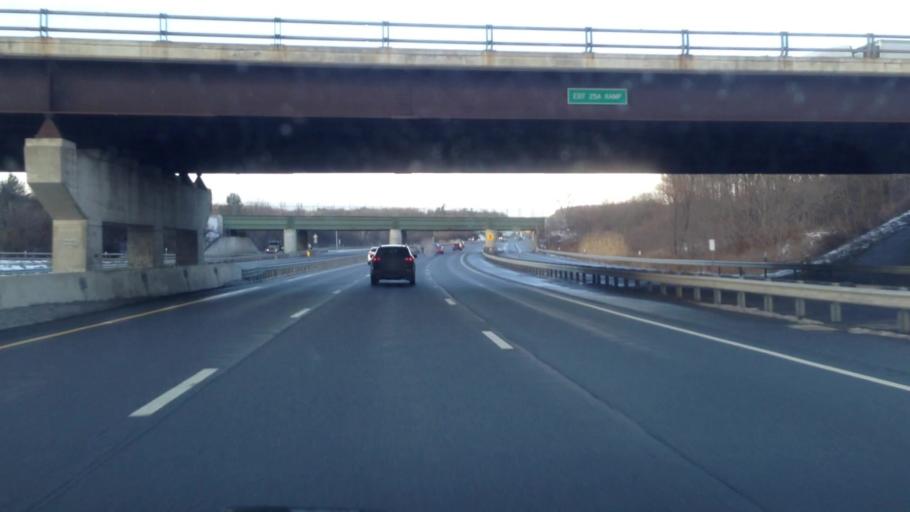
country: US
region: New York
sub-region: Schenectady County
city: Rotterdam
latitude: 42.7903
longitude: -74.0158
